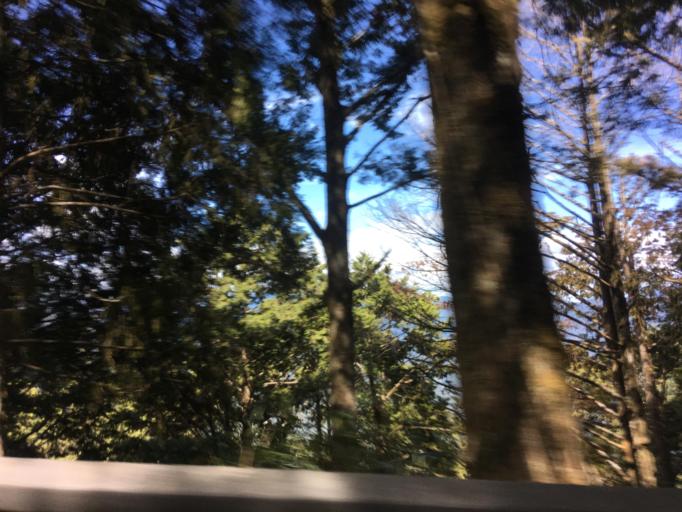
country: TW
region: Taiwan
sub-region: Yilan
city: Yilan
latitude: 24.5048
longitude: 121.5249
